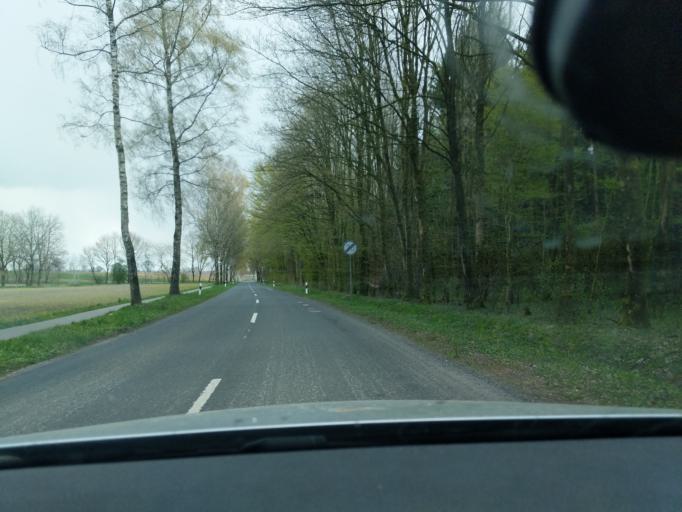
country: DE
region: Lower Saxony
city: Dollern
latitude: 53.5113
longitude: 9.5478
